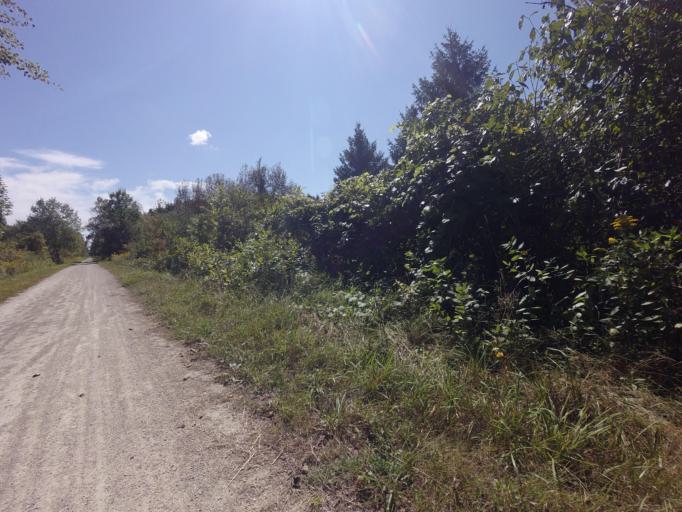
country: CA
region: Ontario
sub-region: Wellington County
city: Guelph
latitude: 43.7375
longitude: -80.3487
